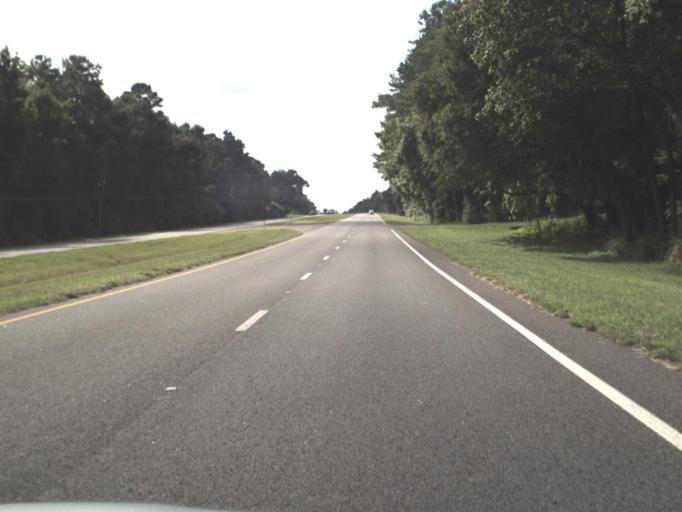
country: US
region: Florida
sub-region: Marion County
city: Citra
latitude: 29.4919
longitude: -82.2538
